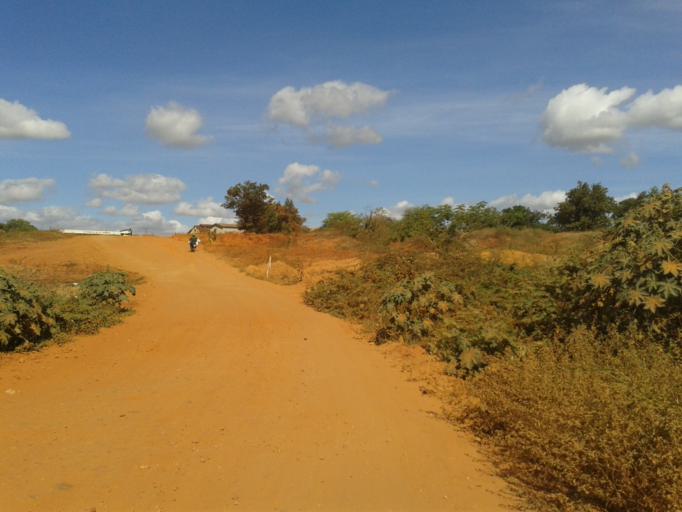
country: BR
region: Bahia
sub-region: Livramento Do Brumado
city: Livramento do Brumado
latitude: -13.6546
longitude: -41.8465
